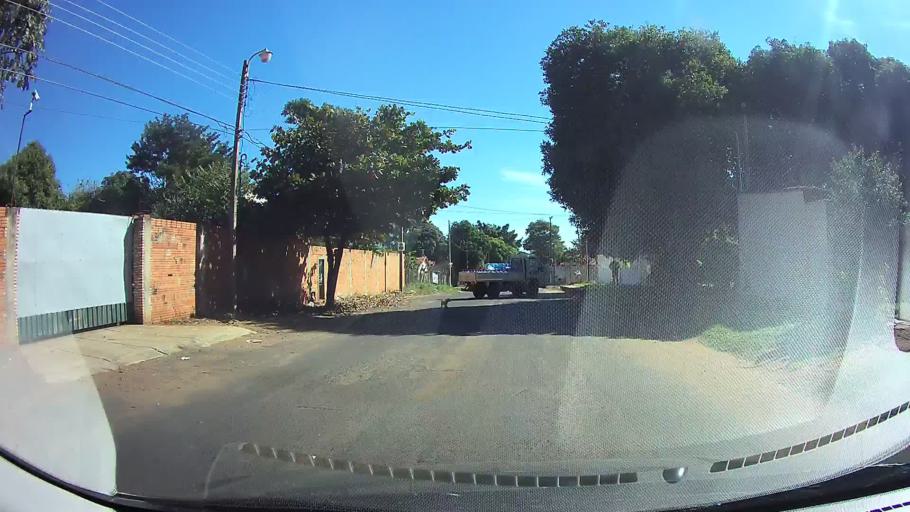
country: PY
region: Central
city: Villa Elisa
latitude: -25.3520
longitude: -57.5757
